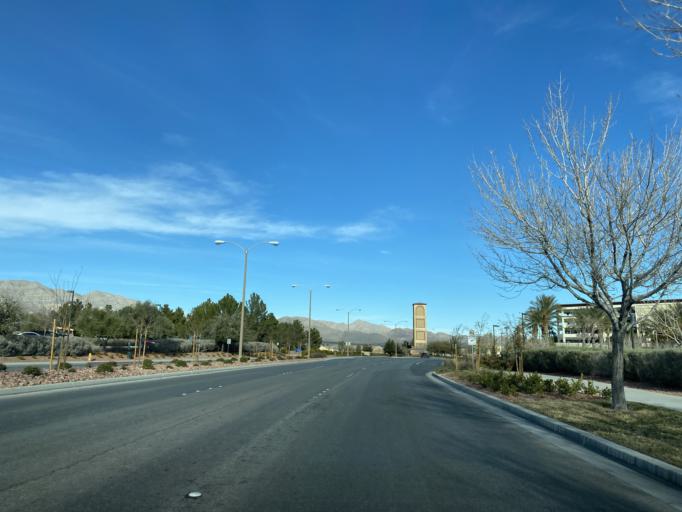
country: US
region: Nevada
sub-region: Clark County
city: North Las Vegas
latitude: 36.2935
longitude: -115.1826
